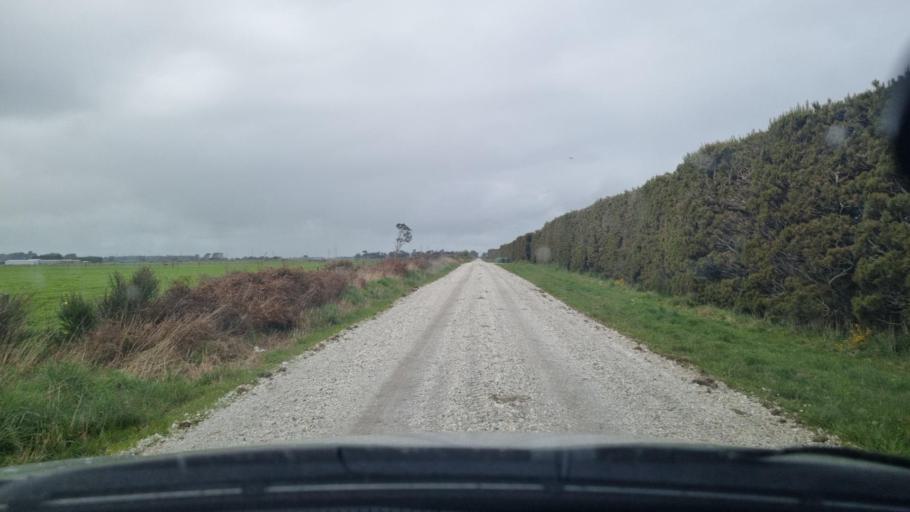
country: NZ
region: Southland
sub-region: Invercargill City
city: Invercargill
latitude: -46.4999
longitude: 168.4110
